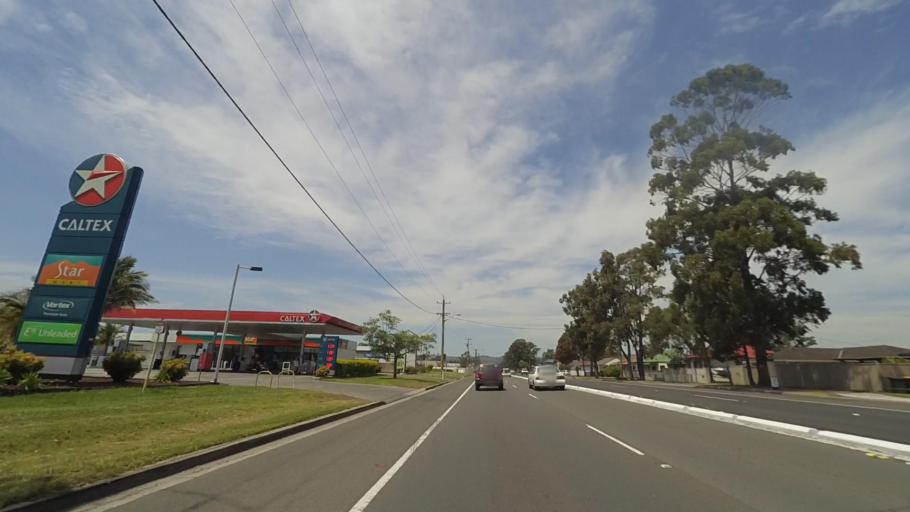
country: AU
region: New South Wales
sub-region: Shellharbour
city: Albion Park Rail
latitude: -34.5516
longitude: 150.7876
